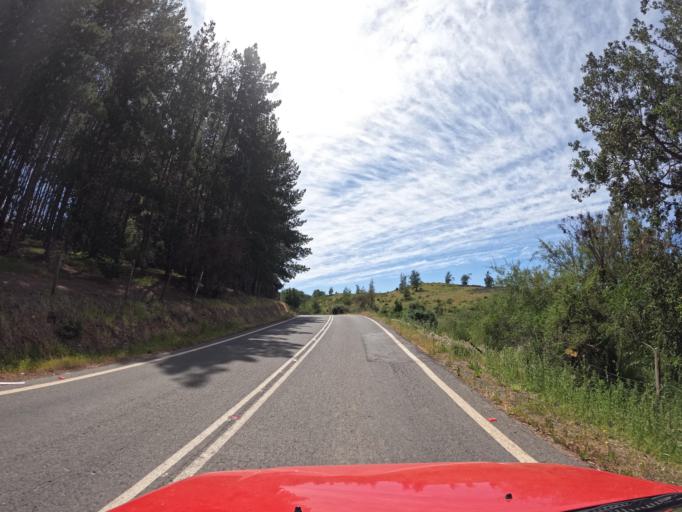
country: CL
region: Maule
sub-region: Provincia de Talca
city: Talca
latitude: -35.0680
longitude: -71.7332
